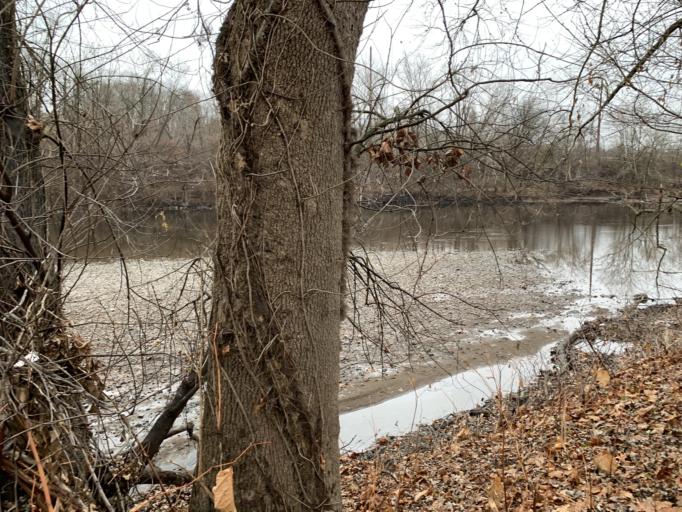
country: US
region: Pennsylvania
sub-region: Montgomery County
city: Sanatoga
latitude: 40.2363
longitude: -75.5973
